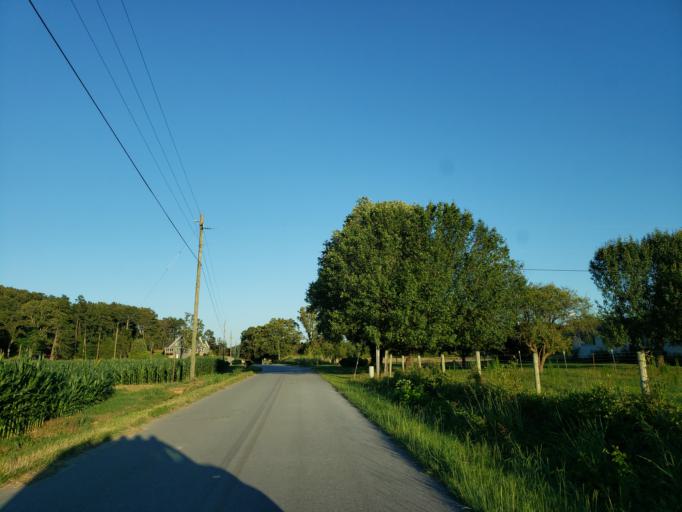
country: US
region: Georgia
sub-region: Bartow County
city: Euharlee
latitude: 34.0738
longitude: -84.9704
